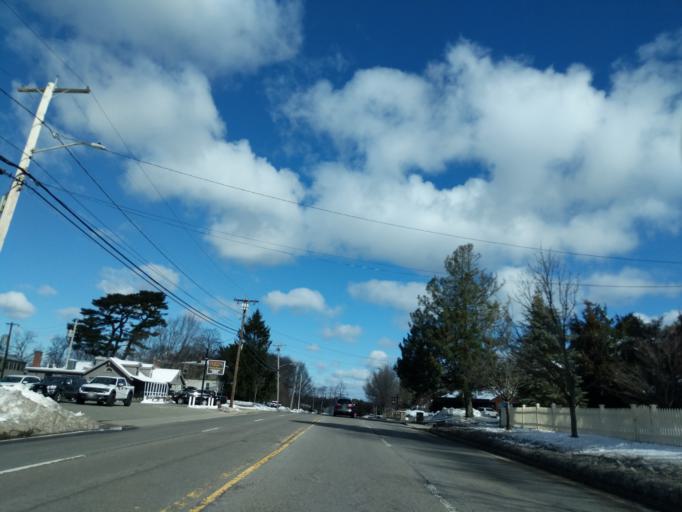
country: US
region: Massachusetts
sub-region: Norfolk County
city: Milton
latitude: 42.2286
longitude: -71.0710
